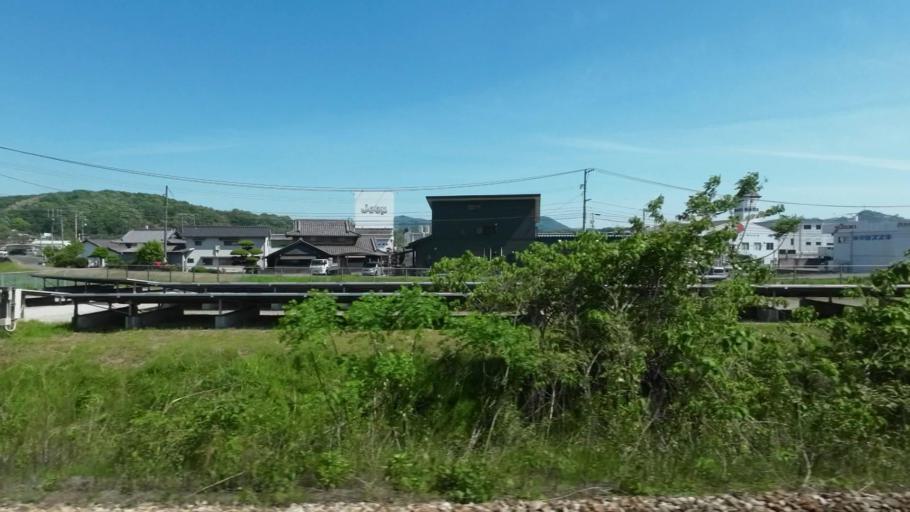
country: JP
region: Hiroshima
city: Fukuyama
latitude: 34.4823
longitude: 133.3222
